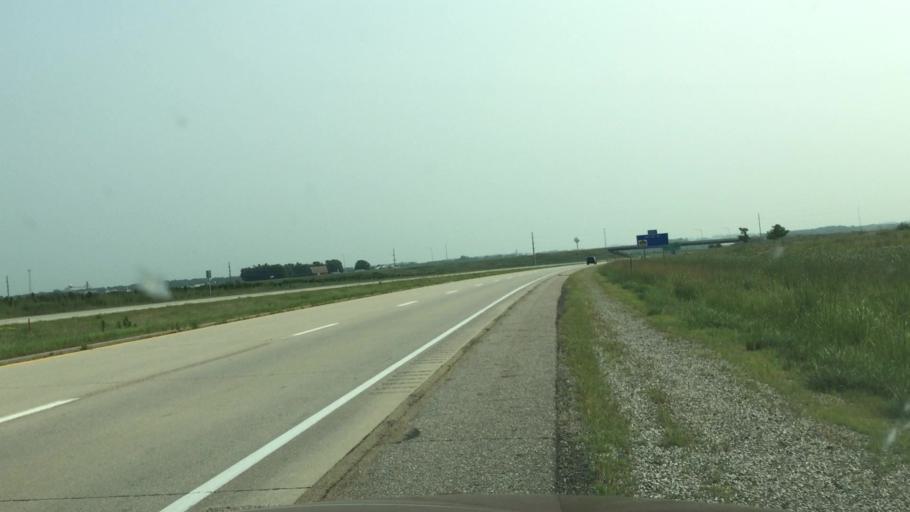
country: US
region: Iowa
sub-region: Osceola County
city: Sibley
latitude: 43.3786
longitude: -95.7567
